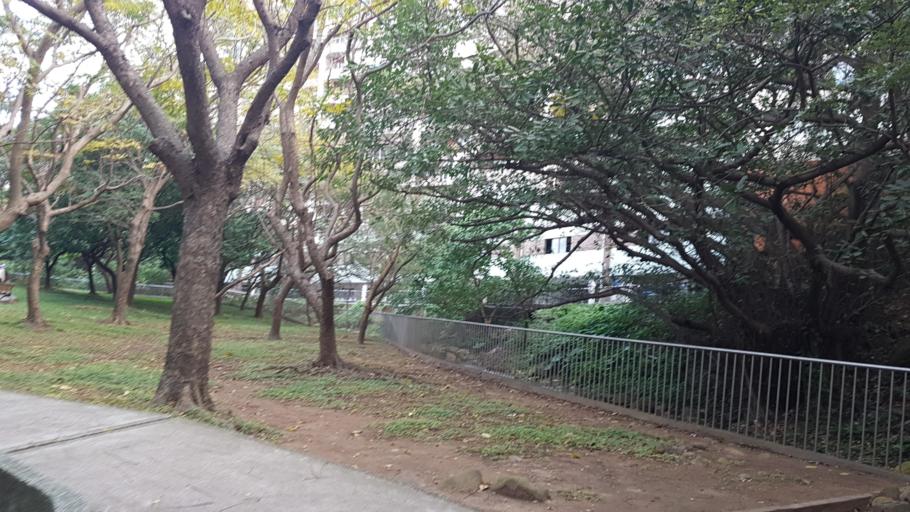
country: TW
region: Taipei
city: Taipei
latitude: 25.1418
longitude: 121.5079
